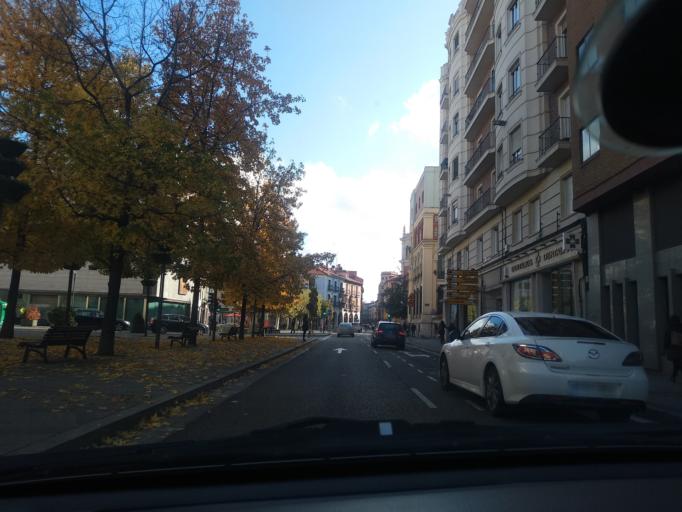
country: ES
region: Castille and Leon
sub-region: Provincia de Valladolid
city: Valladolid
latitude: 41.6535
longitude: -4.7300
